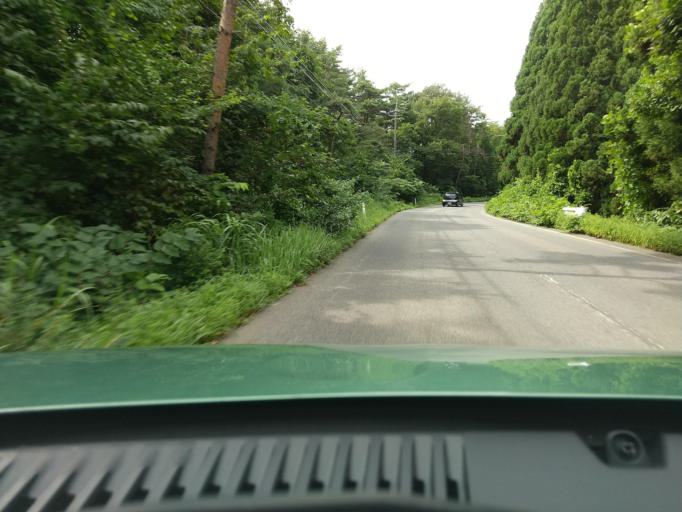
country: JP
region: Akita
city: Akita
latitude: 39.7692
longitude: 140.1342
